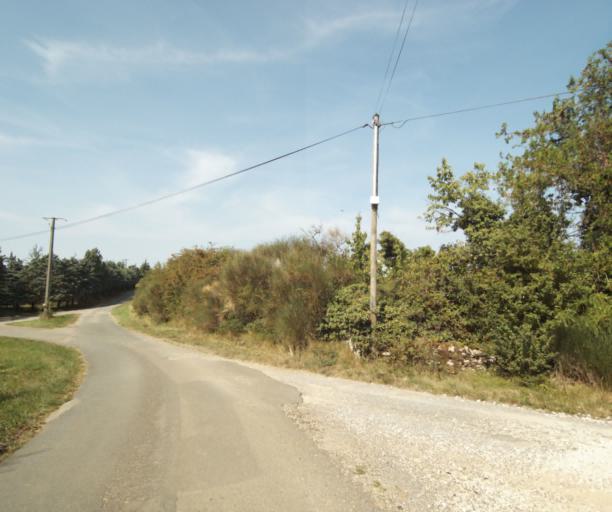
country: FR
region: Bourgogne
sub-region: Departement de Saone-et-Loire
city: Tournus
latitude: 46.5606
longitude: 4.8748
